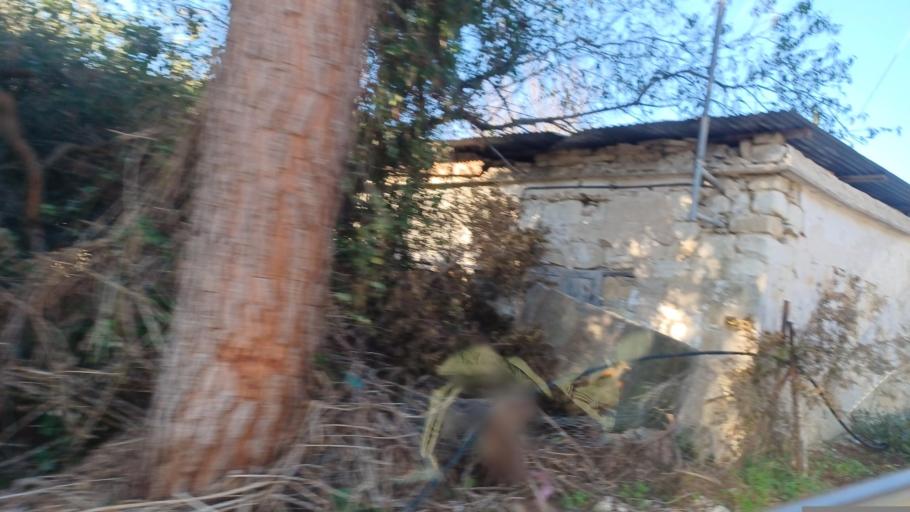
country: CY
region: Pafos
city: Mesogi
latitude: 34.8652
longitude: 32.5562
